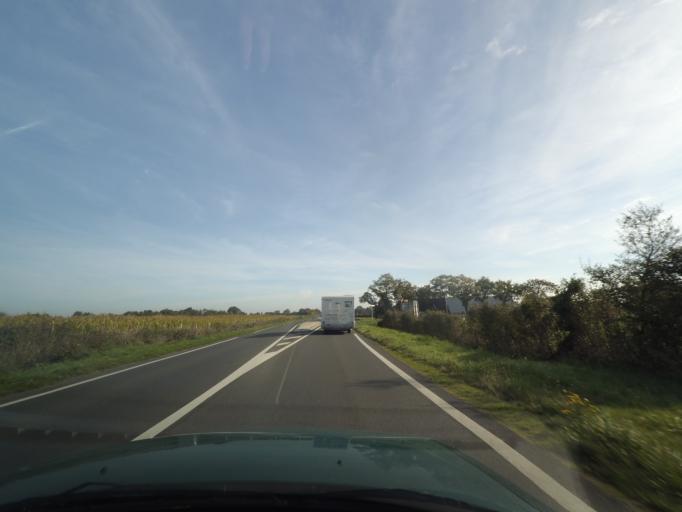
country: FR
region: Pays de la Loire
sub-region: Departement de Maine-et-Loire
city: Torfou
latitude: 47.0354
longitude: -1.0865
